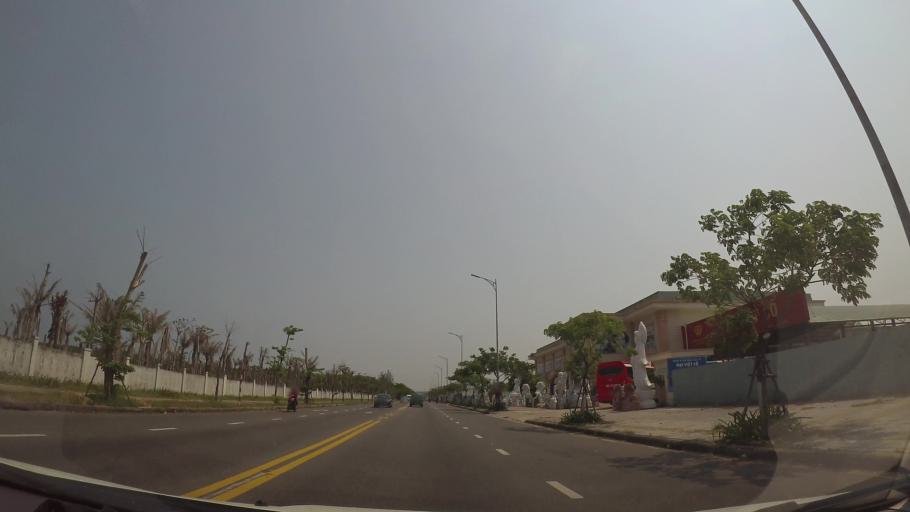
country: VN
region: Da Nang
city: Ngu Hanh Son
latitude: 15.9905
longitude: 108.2705
